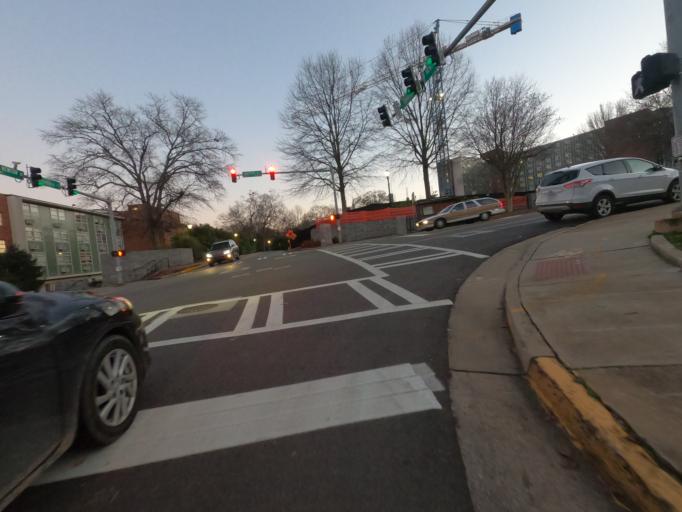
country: US
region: Georgia
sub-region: Clarke County
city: Athens
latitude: 33.9513
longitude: -83.3792
